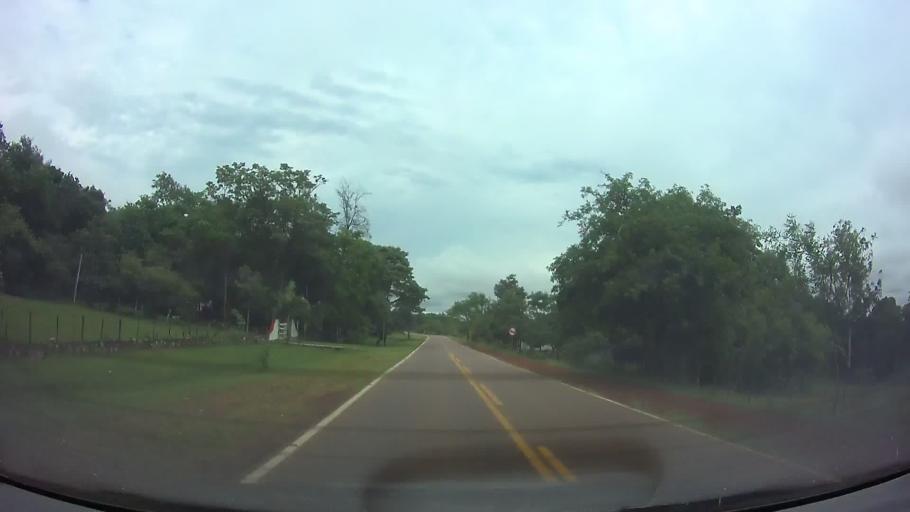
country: PY
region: Paraguari
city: Acahay
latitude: -25.8660
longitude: -57.1281
